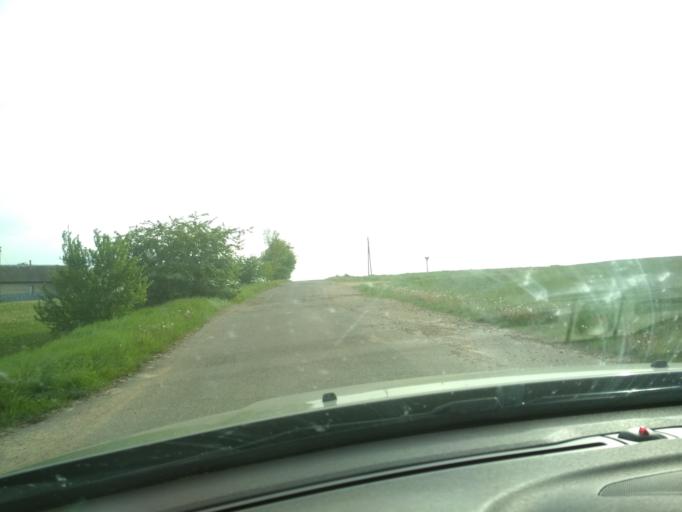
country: BY
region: Grodnenskaya
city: Mir
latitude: 53.4223
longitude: 26.4388
